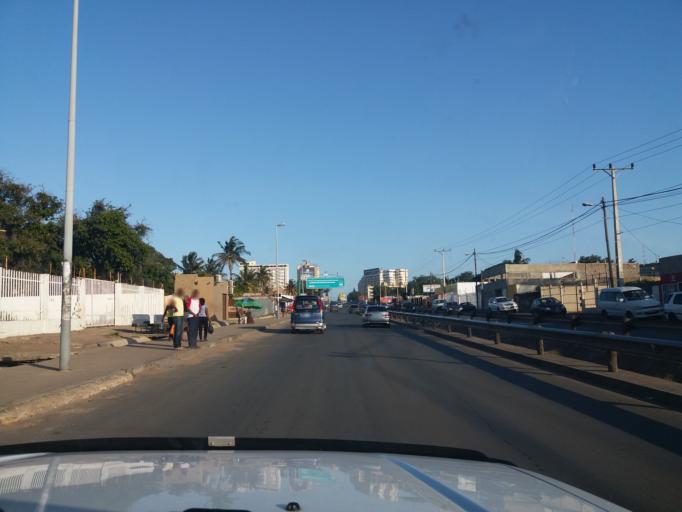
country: MZ
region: Maputo City
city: Maputo
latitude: -25.9495
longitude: 32.5830
